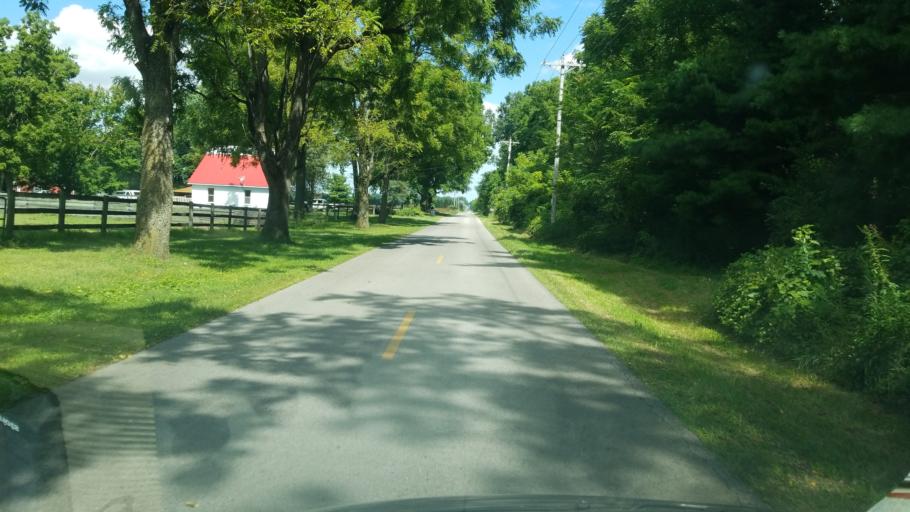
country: US
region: Ohio
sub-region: Henry County
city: Liberty Center
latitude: 41.4781
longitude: -83.9413
